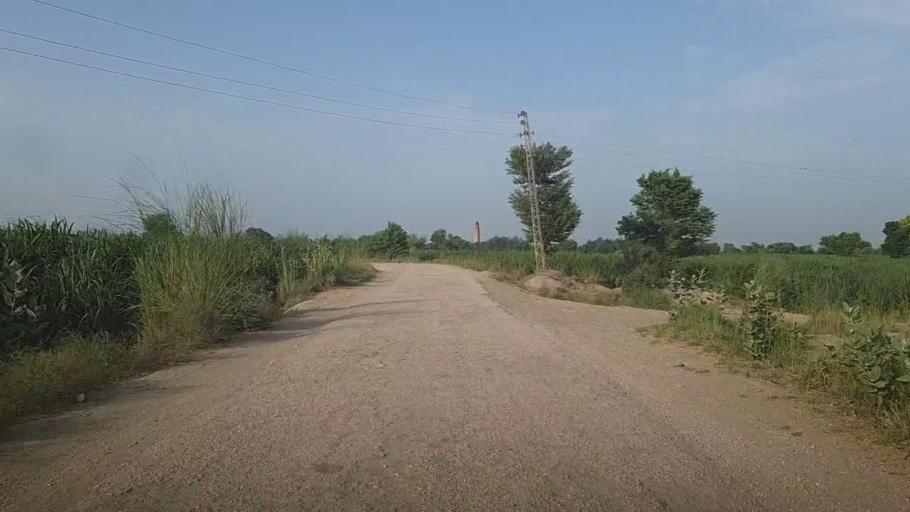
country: PK
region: Sindh
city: Ubauro
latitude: 28.3211
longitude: 69.7949
